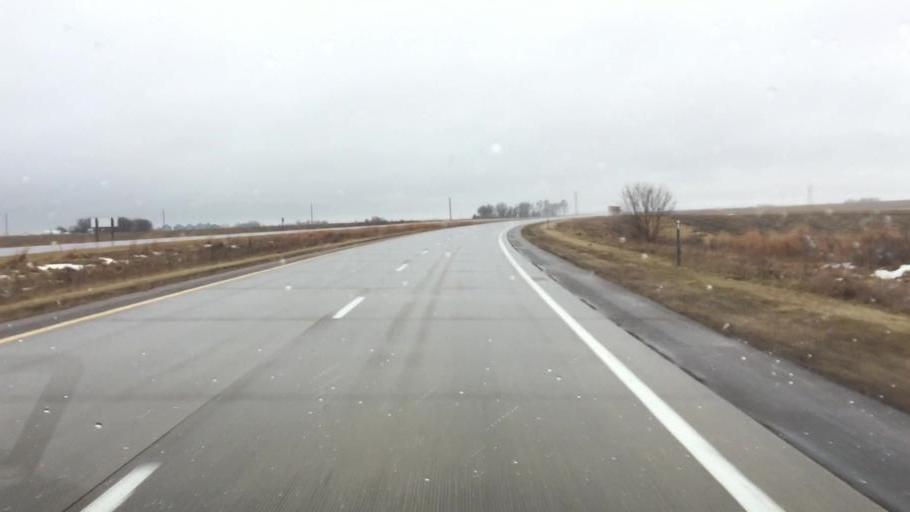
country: US
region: Iowa
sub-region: O'Brien County
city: Sheldon
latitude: 43.0676
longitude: -95.8972
